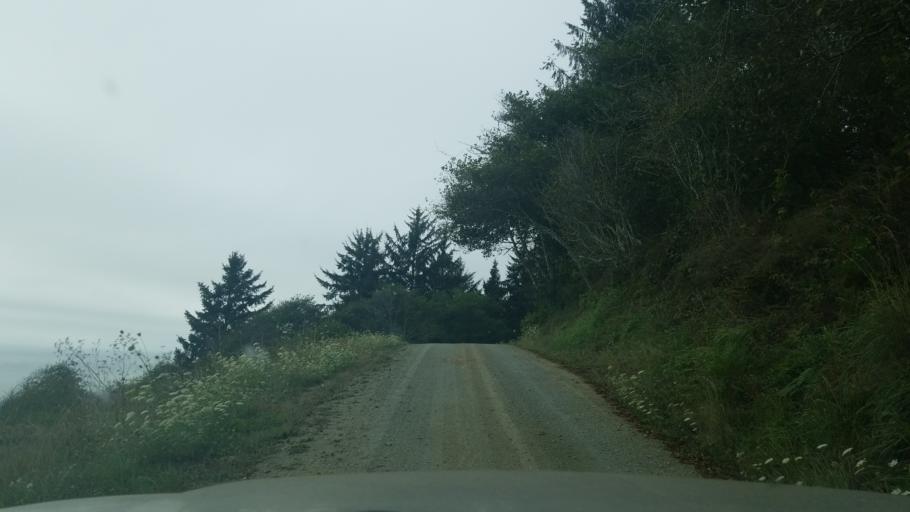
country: US
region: California
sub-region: Del Norte County
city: Bertsch-Oceanview
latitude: 41.5239
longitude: -124.0791
